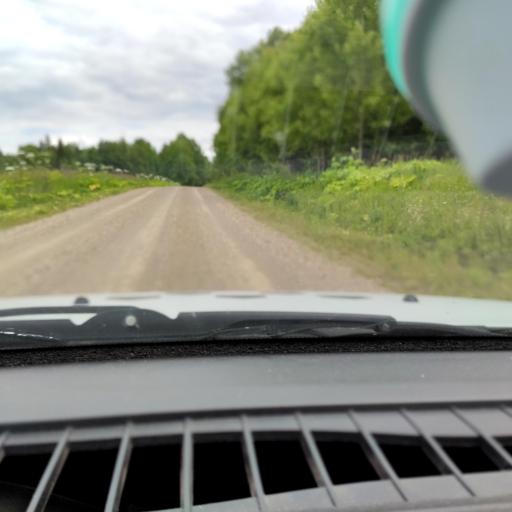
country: RU
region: Perm
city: Suksun
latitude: 57.2092
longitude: 57.6483
